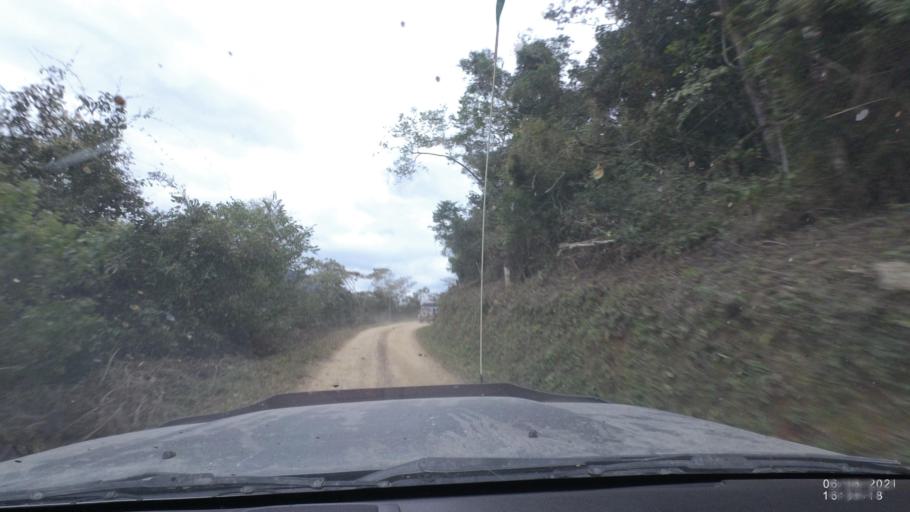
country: BO
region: La Paz
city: Quime
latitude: -16.5264
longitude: -66.7658
